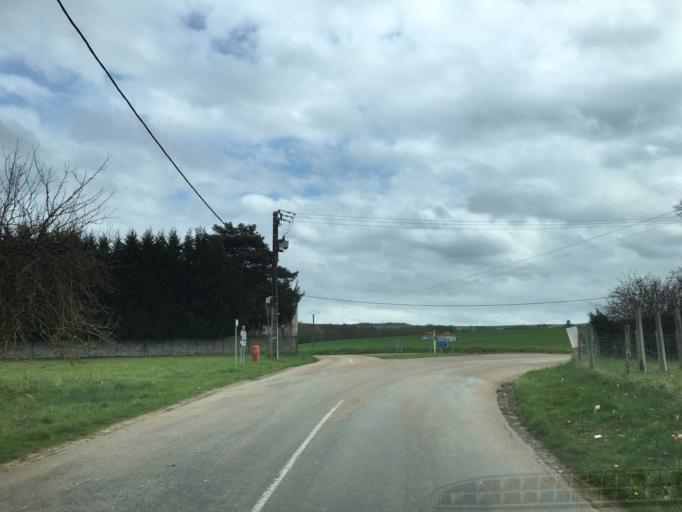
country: FR
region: Bourgogne
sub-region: Departement de l'Yonne
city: Pourrain
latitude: 47.7924
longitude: 3.3890
